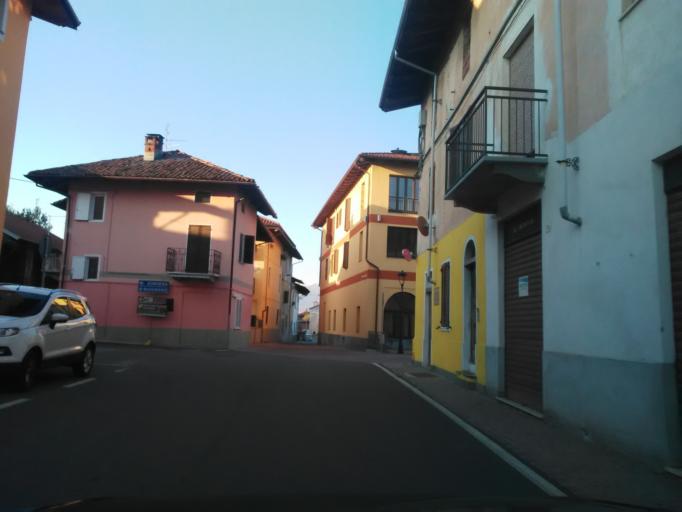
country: IT
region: Piedmont
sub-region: Provincia di Biella
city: Cerrione
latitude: 45.4681
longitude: 8.0694
